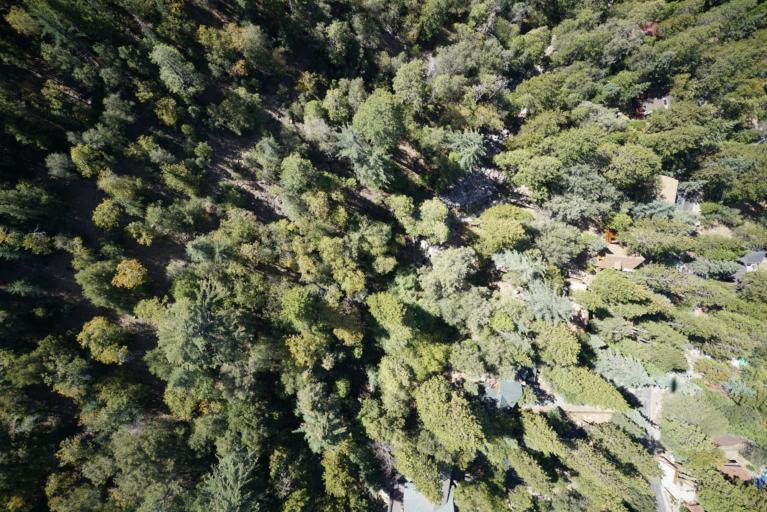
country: US
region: California
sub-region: Riverside County
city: Idyllwild
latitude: 33.7634
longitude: -116.6899
